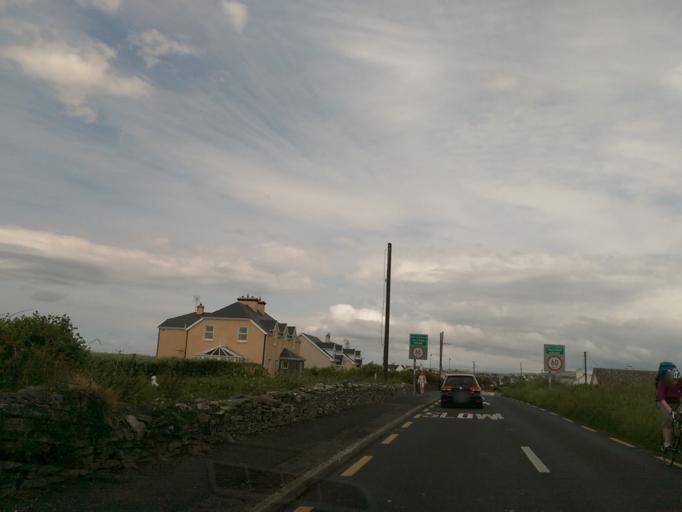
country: IE
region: Munster
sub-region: An Clar
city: Kilrush
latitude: 52.8482
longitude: -9.4153
